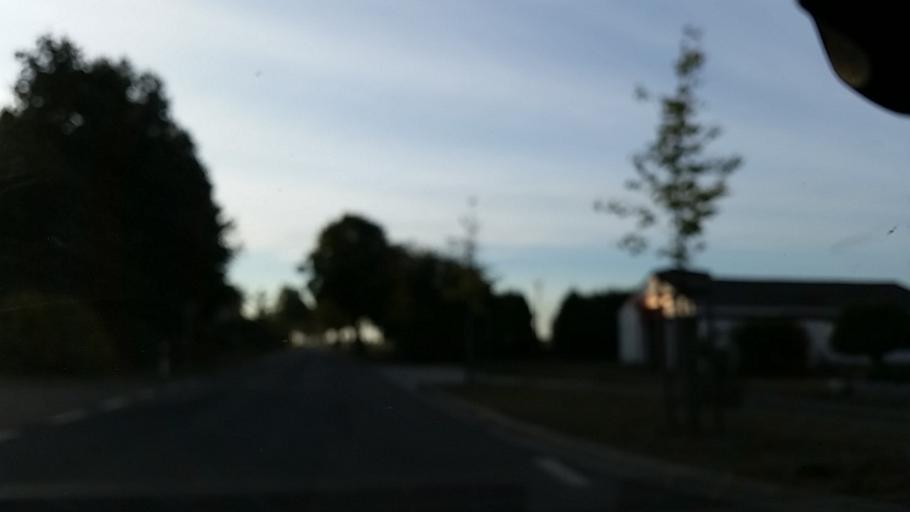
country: DE
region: Lower Saxony
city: Wittingen
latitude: 52.7589
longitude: 10.7105
